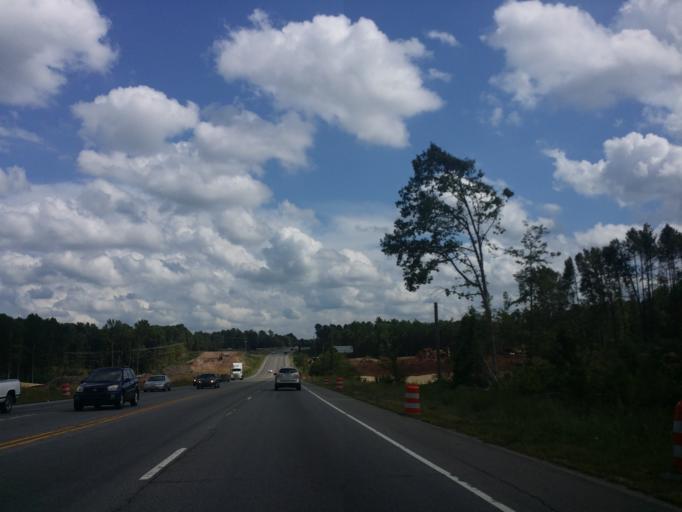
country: US
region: North Carolina
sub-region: Durham County
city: Durham
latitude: 35.9754
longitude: -78.8539
